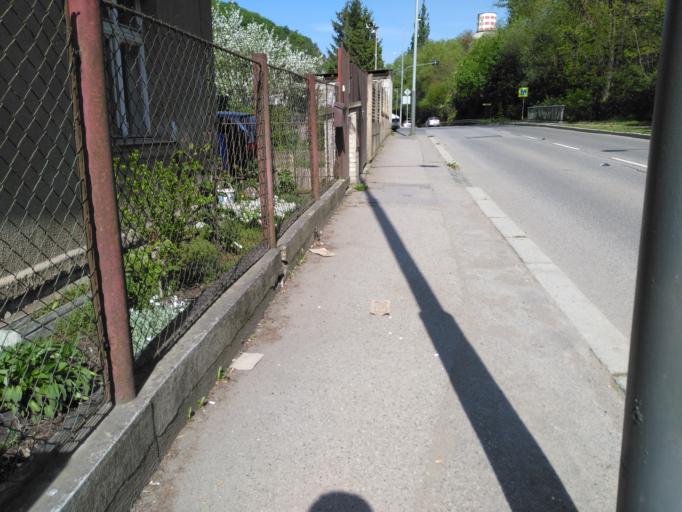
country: CZ
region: Central Bohemia
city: Cernosice
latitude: 49.9924
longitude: 14.3457
